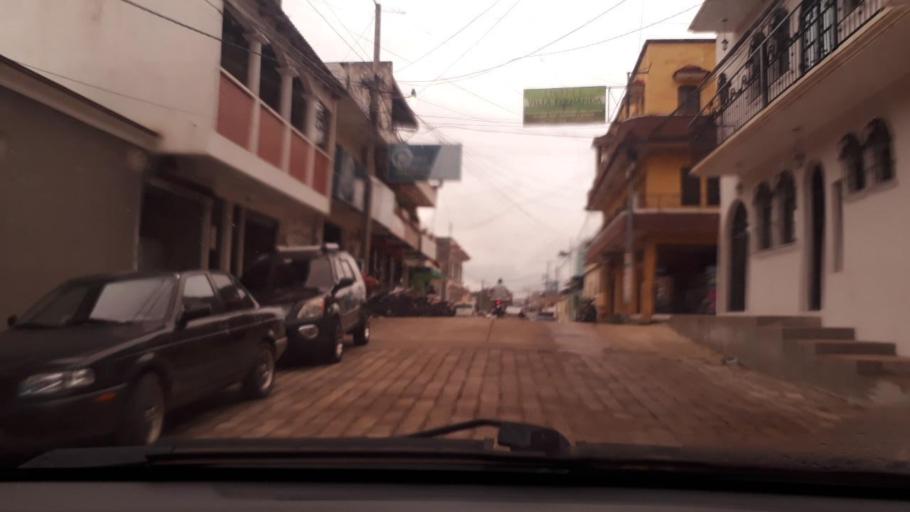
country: GT
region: Chiquimula
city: Esquipulas
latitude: 14.5629
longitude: -89.3550
